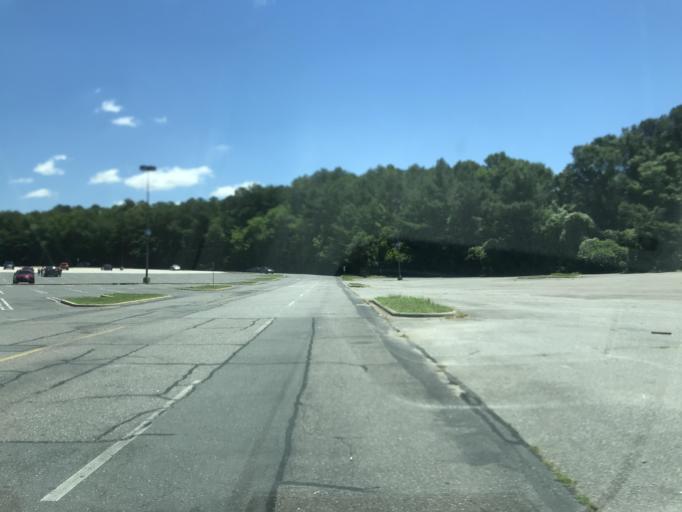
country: US
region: North Carolina
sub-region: Gaston County
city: Ranlo
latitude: 35.2631
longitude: -81.1489
